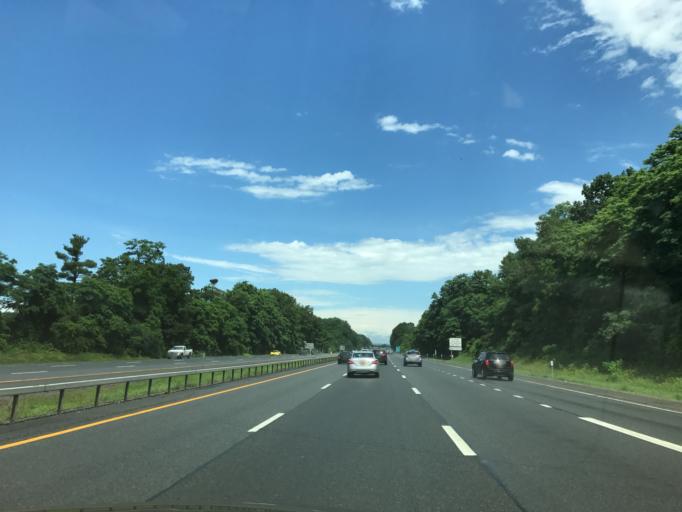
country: US
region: New York
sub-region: Saratoga County
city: Country Knolls
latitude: 42.8647
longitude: -73.7754
